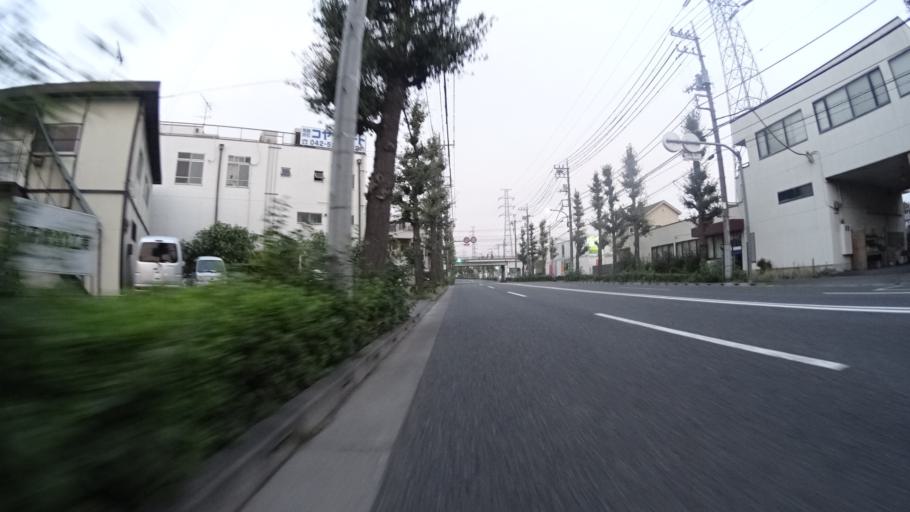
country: JP
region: Tokyo
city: Hino
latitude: 35.6895
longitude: 139.4009
